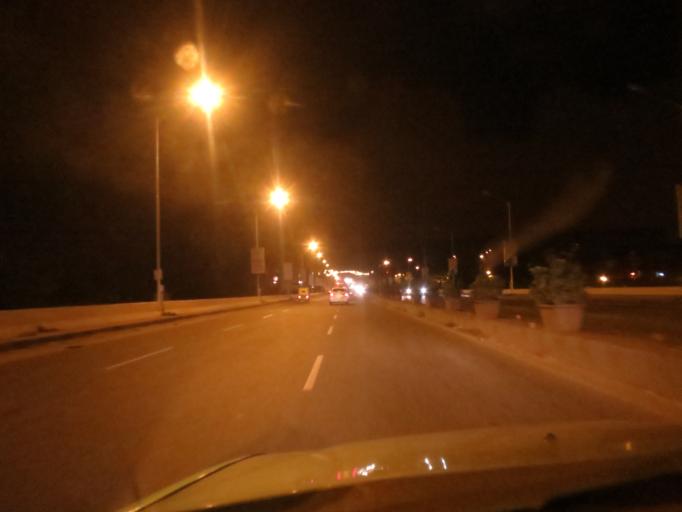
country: IN
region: Karnataka
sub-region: Bangalore Urban
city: Bangalore
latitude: 12.9989
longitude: 77.6635
